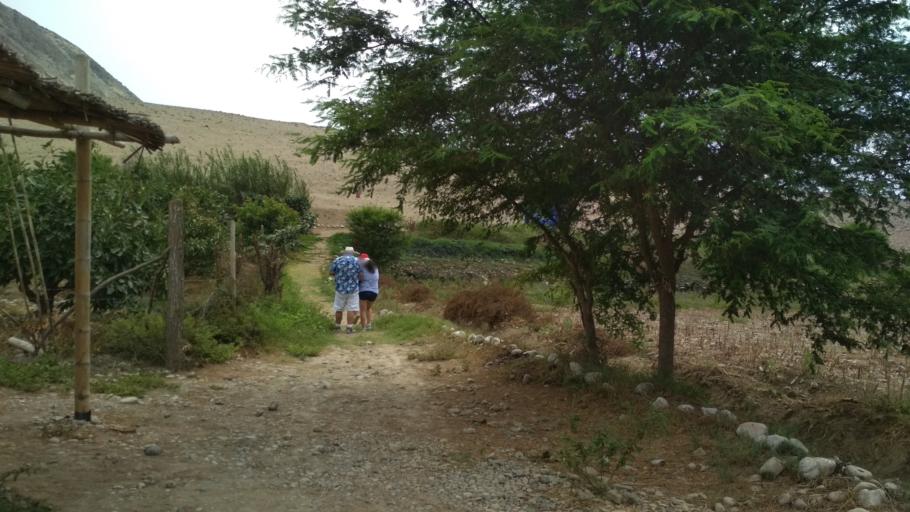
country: PE
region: Lima
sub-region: Huaura
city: Vegueta
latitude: -10.8917
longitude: -77.5160
